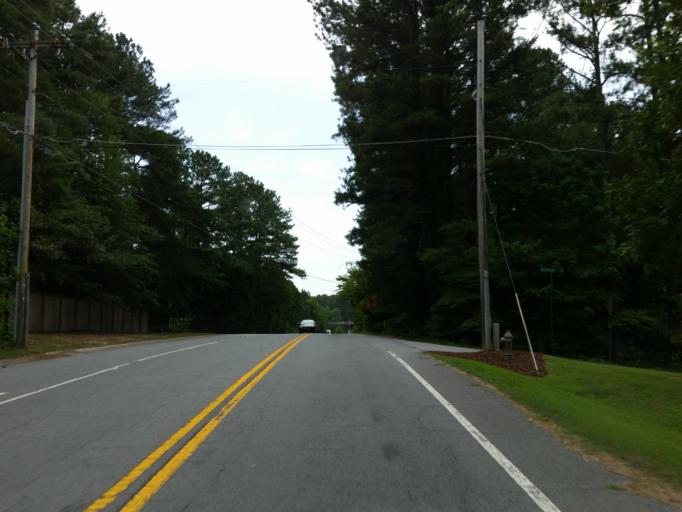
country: US
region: Georgia
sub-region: Cobb County
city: Marietta
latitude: 33.9857
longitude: -84.4776
